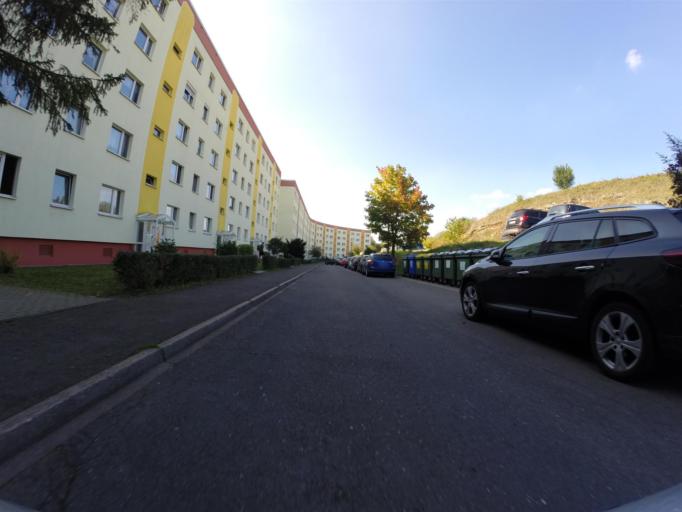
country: DE
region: Thuringia
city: Zollnitz
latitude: 50.8824
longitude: 11.6324
